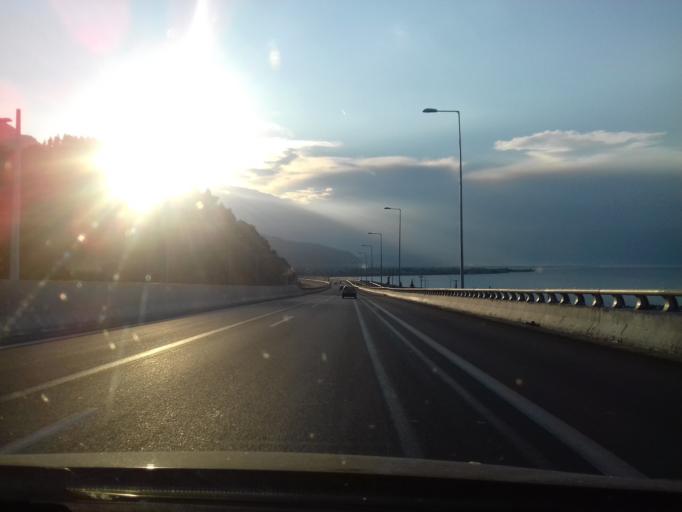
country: GR
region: West Greece
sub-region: Nomos Achaias
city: Akrata
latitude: 38.1755
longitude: 22.2414
